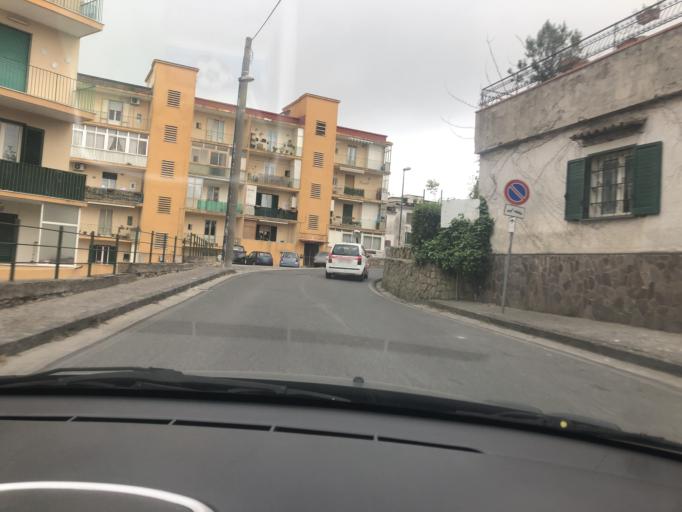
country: IT
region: Campania
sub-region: Provincia di Napoli
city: Torre Caracciolo
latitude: 40.8647
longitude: 14.1900
